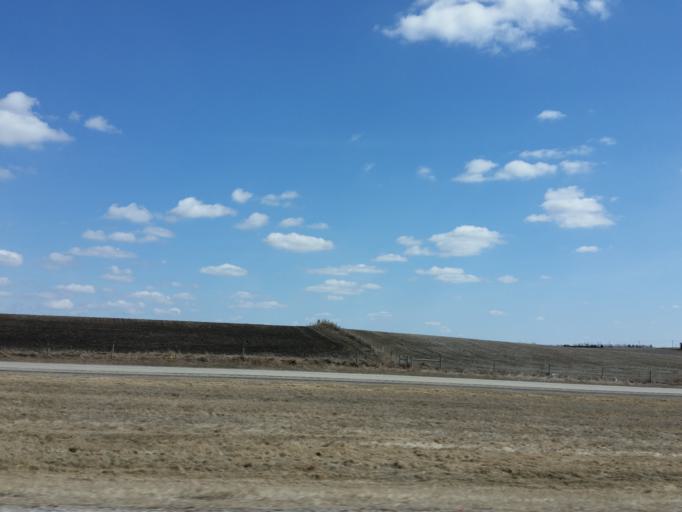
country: US
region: South Dakota
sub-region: Codington County
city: Watertown
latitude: 44.9085
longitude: -97.0566
